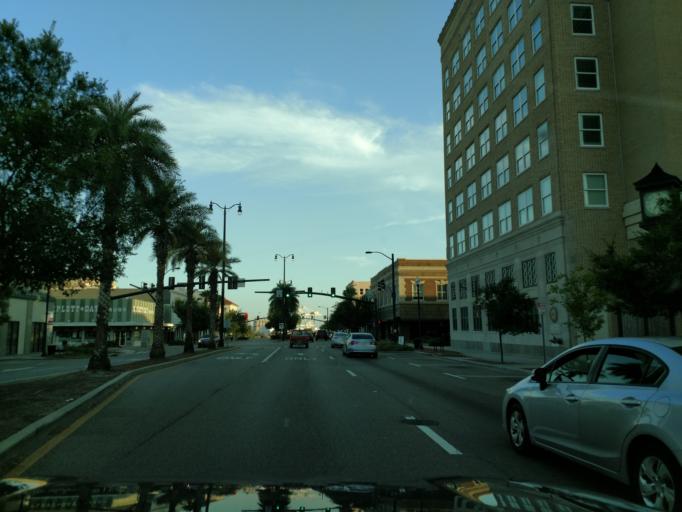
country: US
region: Mississippi
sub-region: Harrison County
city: Gulfport
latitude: 30.3688
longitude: -89.0930
